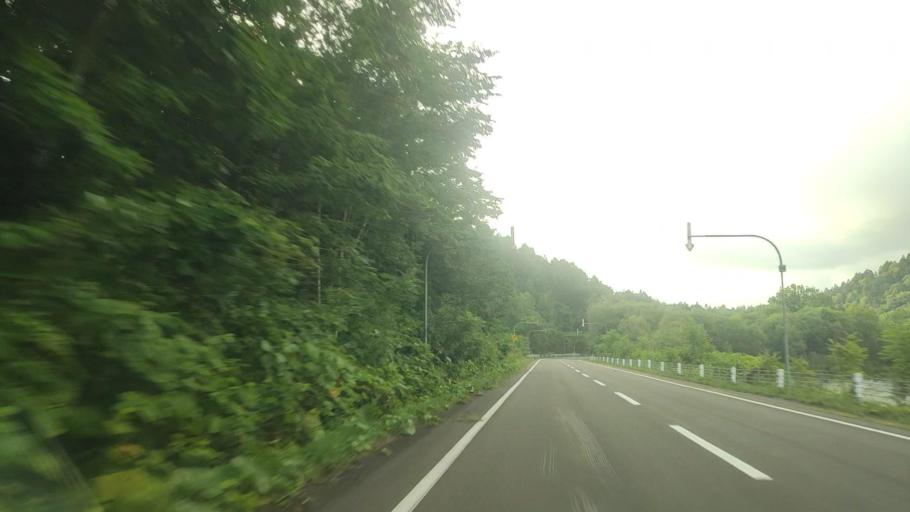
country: JP
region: Hokkaido
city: Bibai
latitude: 43.1244
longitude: 142.1024
